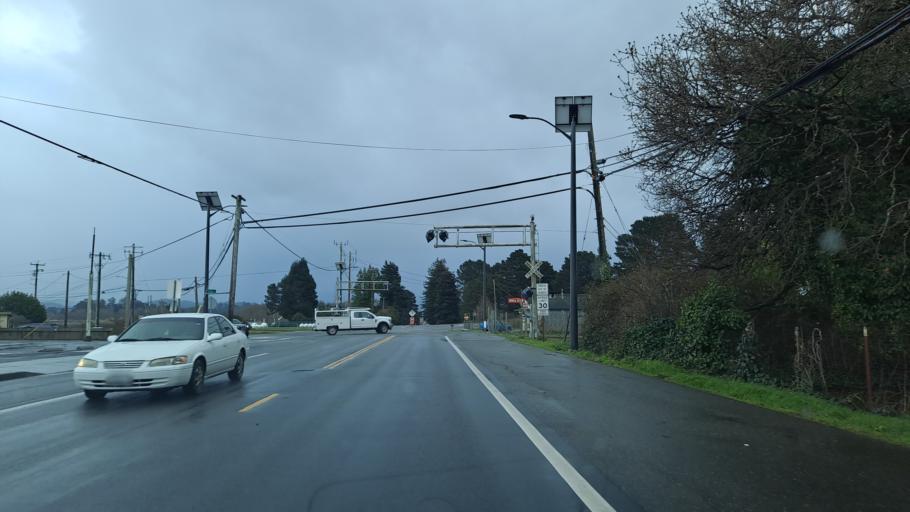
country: US
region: California
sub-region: Humboldt County
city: Fortuna
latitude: 40.5904
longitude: -124.1546
